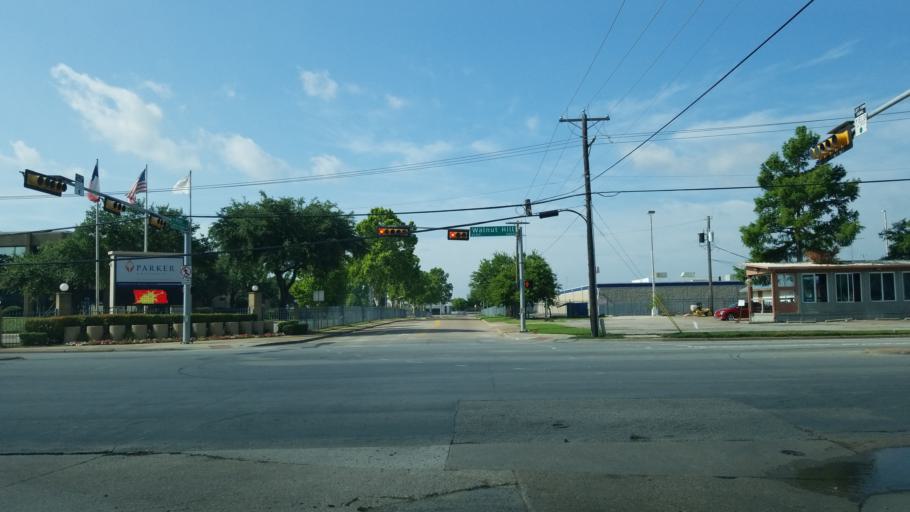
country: US
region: Texas
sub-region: Dallas County
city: Farmers Branch
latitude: 32.8813
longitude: -96.8943
